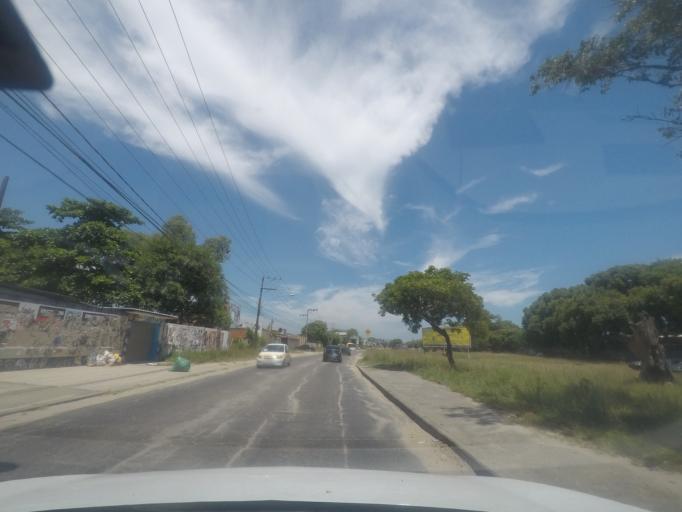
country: BR
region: Rio de Janeiro
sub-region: Itaguai
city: Itaguai
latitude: -22.9781
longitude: -43.6710
